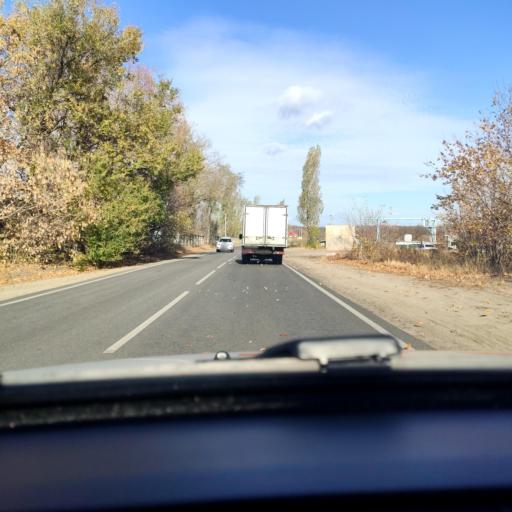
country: RU
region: Voronezj
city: Shilovo
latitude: 51.5622
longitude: 39.1402
